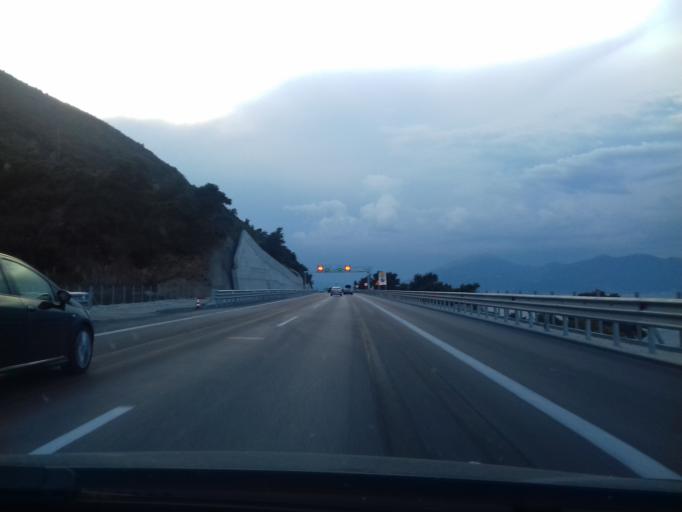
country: GR
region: West Greece
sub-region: Nomos Achaias
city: Kamarai
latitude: 38.3216
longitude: 21.9681
